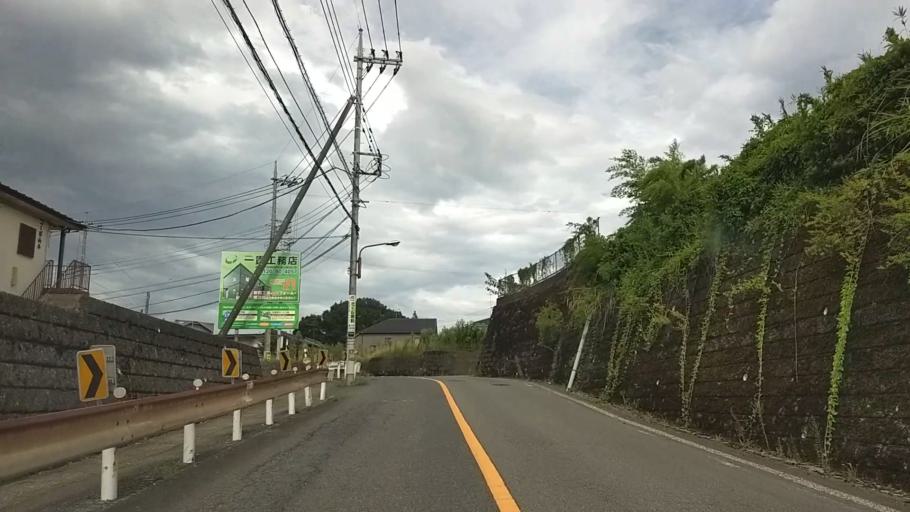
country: JP
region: Tokyo
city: Hachioji
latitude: 35.6429
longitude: 139.3476
